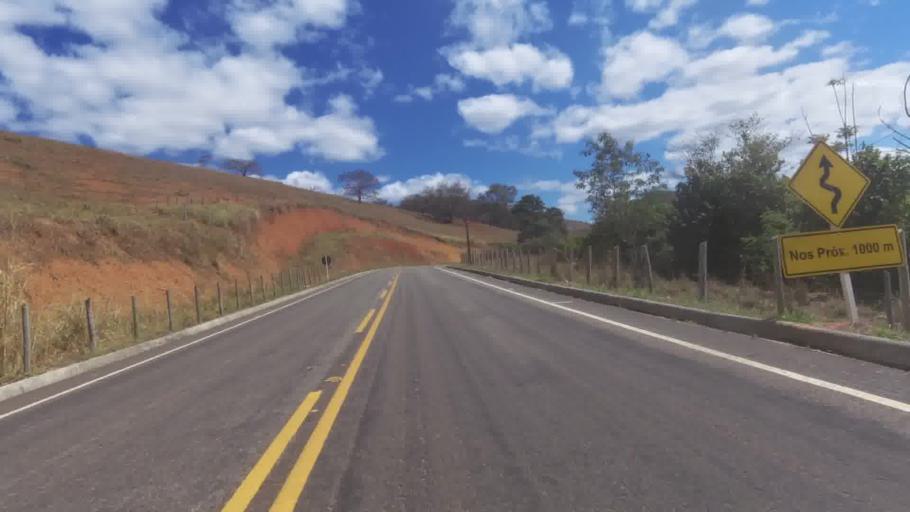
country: BR
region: Espirito Santo
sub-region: Cachoeiro De Itapemirim
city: Cachoeiro de Itapemirim
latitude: -20.9142
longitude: -41.2365
